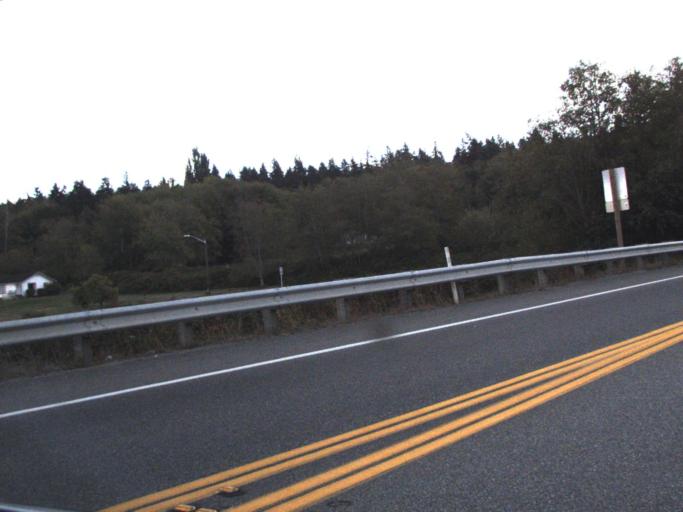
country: US
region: Washington
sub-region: Island County
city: Ault Field
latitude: 48.3488
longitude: -122.6125
